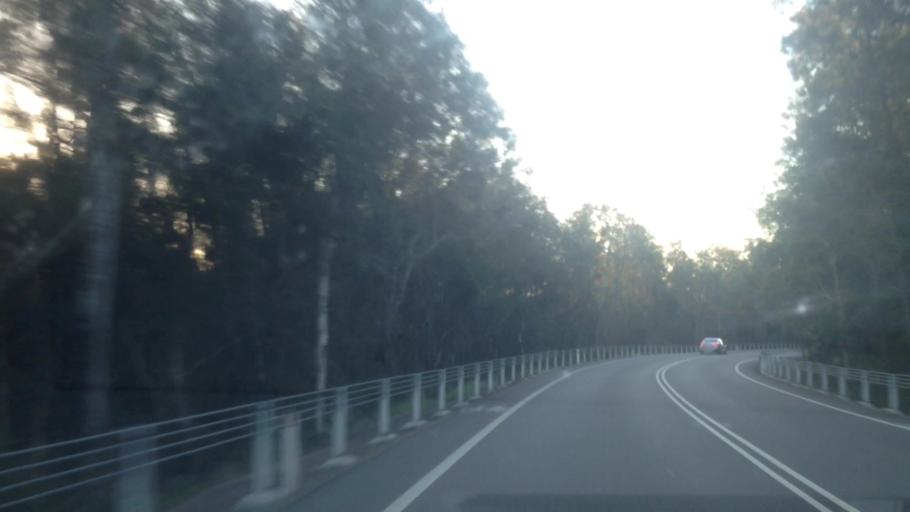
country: AU
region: New South Wales
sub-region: Wyong Shire
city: Kingfisher Shores
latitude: -33.1613
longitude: 151.5291
